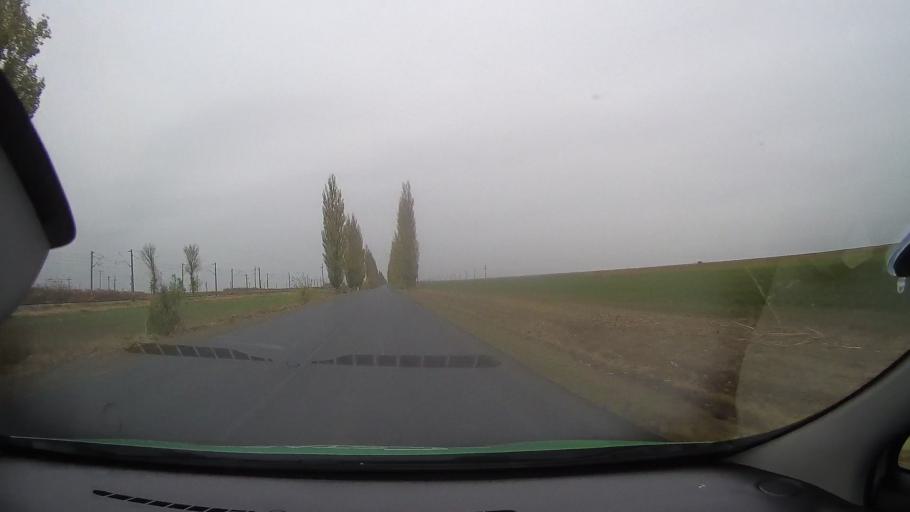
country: RO
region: Ialomita
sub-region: Comuna Valea Ciorii
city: Valea Ciorii
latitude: 44.7115
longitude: 27.5919
